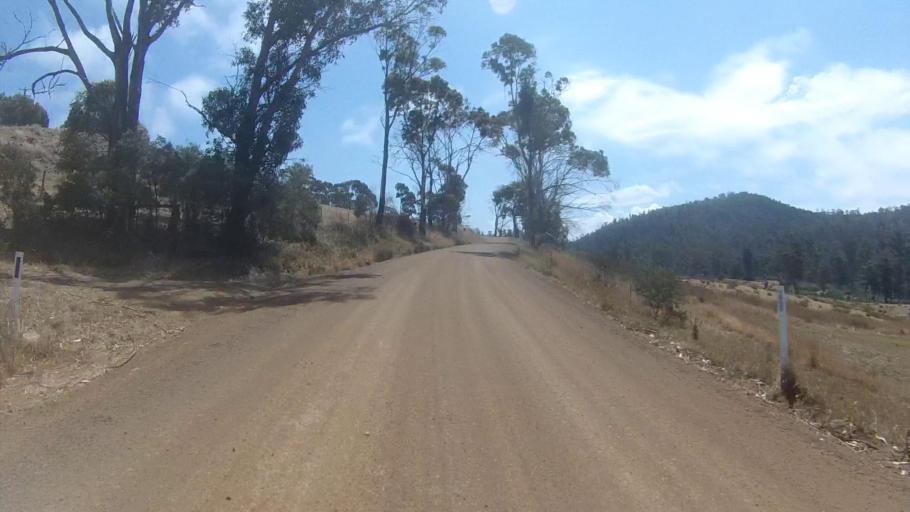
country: AU
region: Tasmania
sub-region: Sorell
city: Sorell
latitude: -42.8531
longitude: 147.8264
